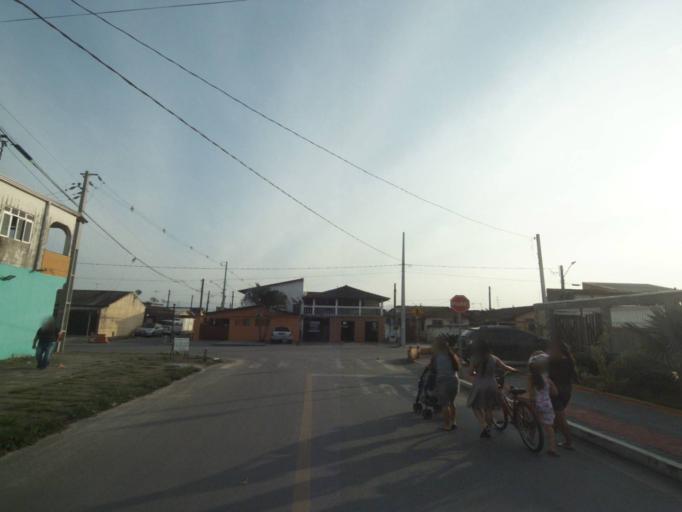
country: BR
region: Parana
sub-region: Paranagua
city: Paranagua
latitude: -25.5175
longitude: -48.5427
